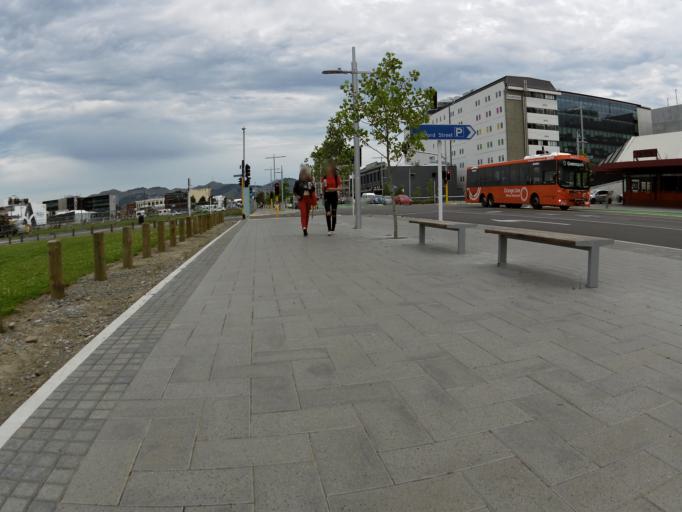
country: NZ
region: Canterbury
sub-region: Christchurch City
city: Christchurch
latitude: -43.5316
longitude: 172.6398
